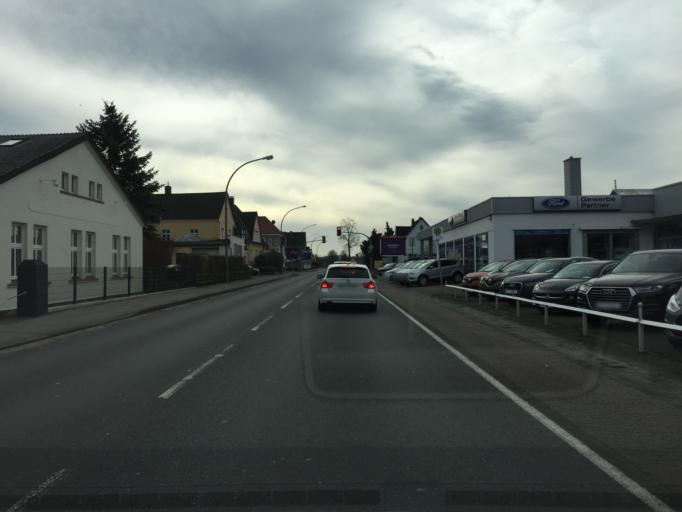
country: DE
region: North Rhine-Westphalia
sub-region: Regierungsbezirk Detmold
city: Lage
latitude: 52.0259
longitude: 8.7596
